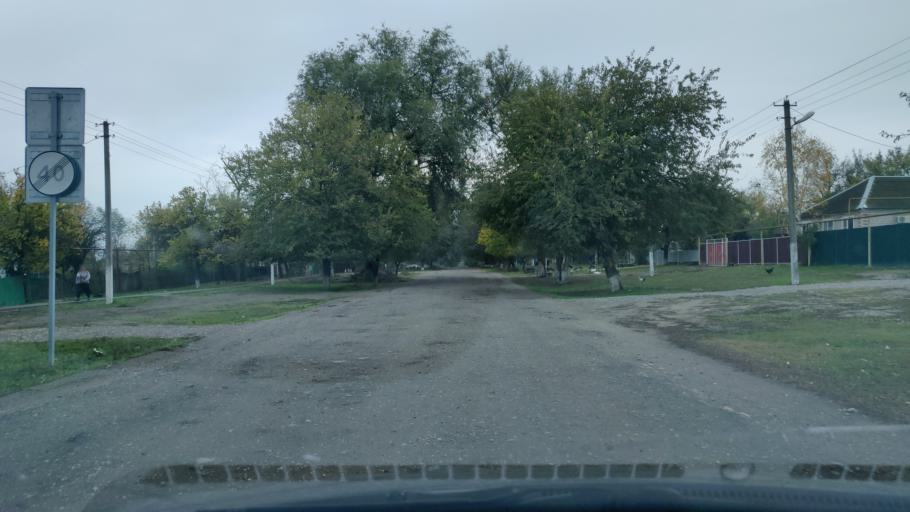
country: RU
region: Stavropol'skiy
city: Irgakly
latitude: 44.2435
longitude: 44.7207
